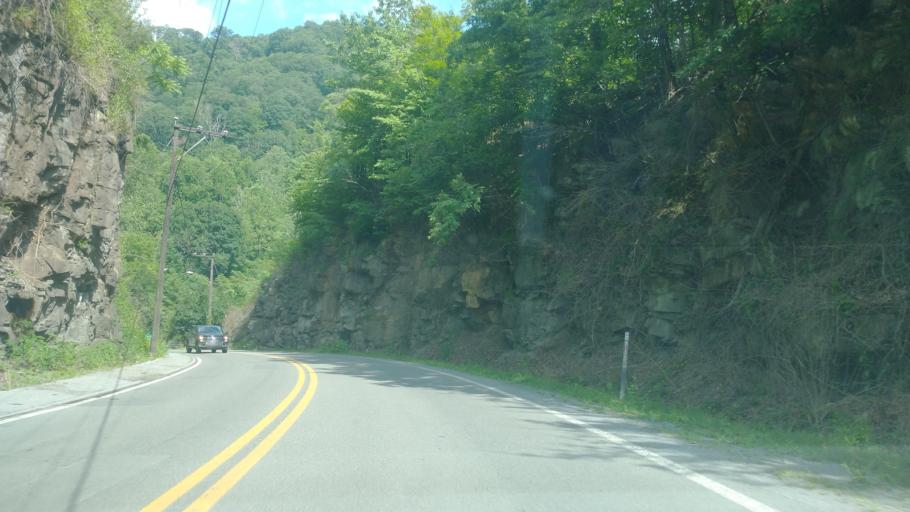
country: US
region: West Virginia
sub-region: McDowell County
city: Welch
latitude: 37.4206
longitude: -81.4411
